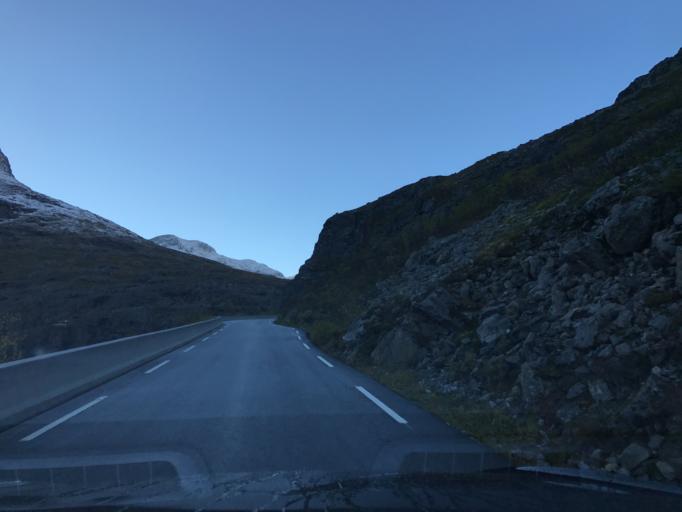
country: NO
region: More og Romsdal
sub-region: Rauma
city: Andalsnes
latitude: 62.4609
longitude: 7.6661
